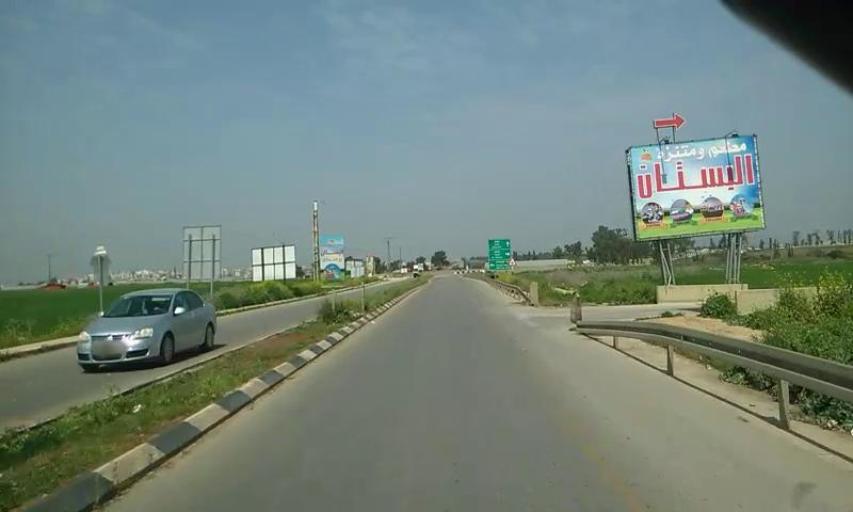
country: PS
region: West Bank
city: Al Jalamah
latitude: 32.5019
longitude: 35.3021
